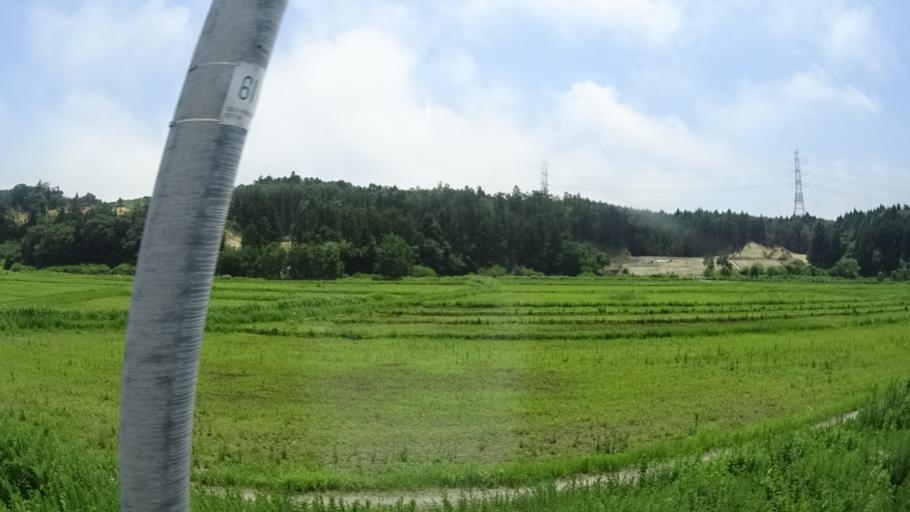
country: JP
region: Fukushima
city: Namie
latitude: 37.3221
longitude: 141.0138
